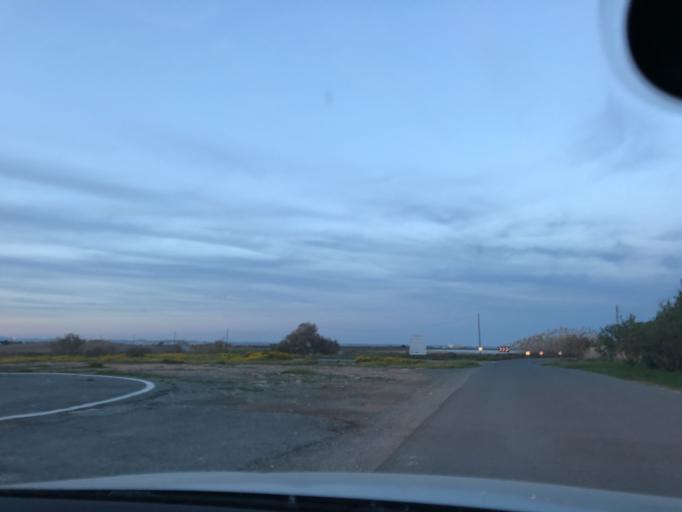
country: CY
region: Larnaka
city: Meneou
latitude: 34.8620
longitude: 33.6326
